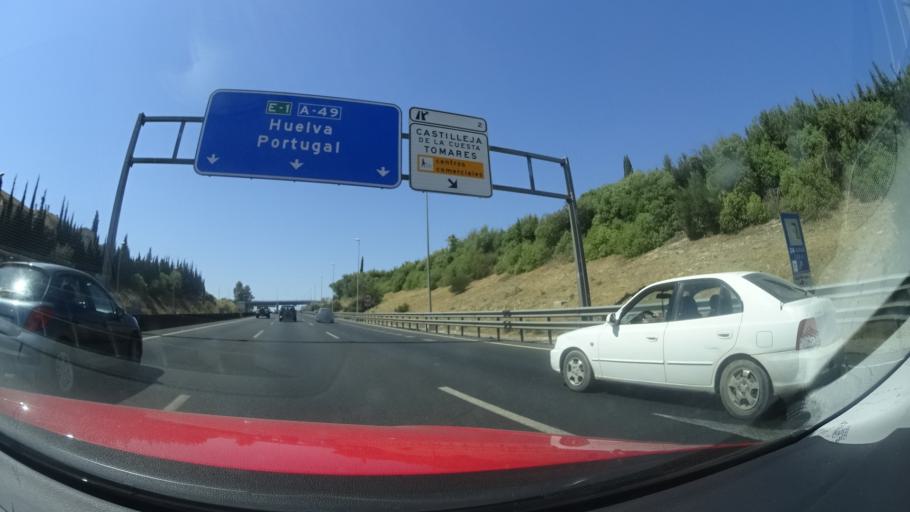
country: ES
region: Andalusia
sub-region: Provincia de Sevilla
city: Tomares
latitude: 37.3812
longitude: -6.0418
